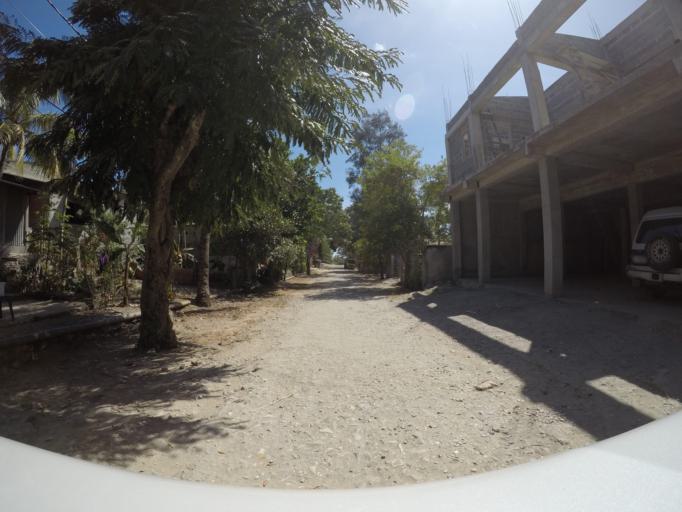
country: TL
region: Baucau
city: Baucau
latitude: -8.4769
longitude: 126.4534
